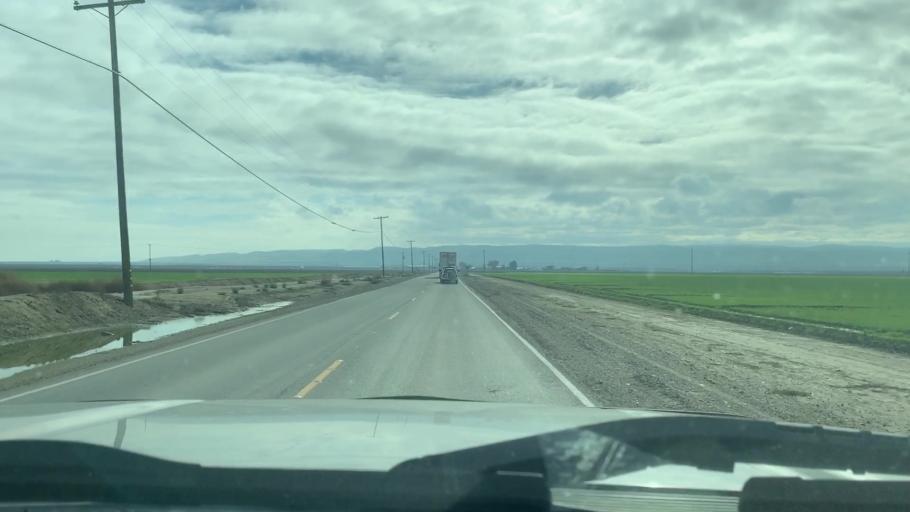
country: US
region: California
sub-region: Merced County
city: Los Banos
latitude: 36.9724
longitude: -120.8375
